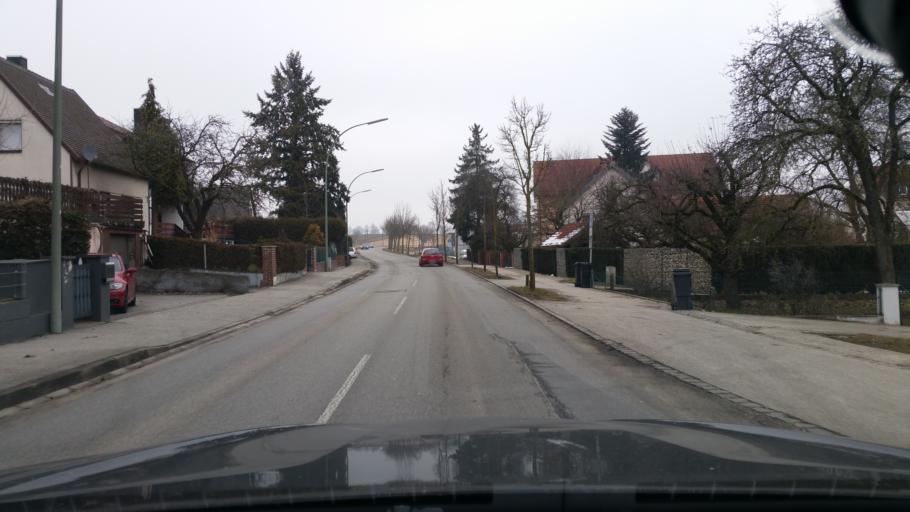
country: DE
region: Bavaria
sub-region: Lower Bavaria
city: Ergolding
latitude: 48.5628
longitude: 12.1349
